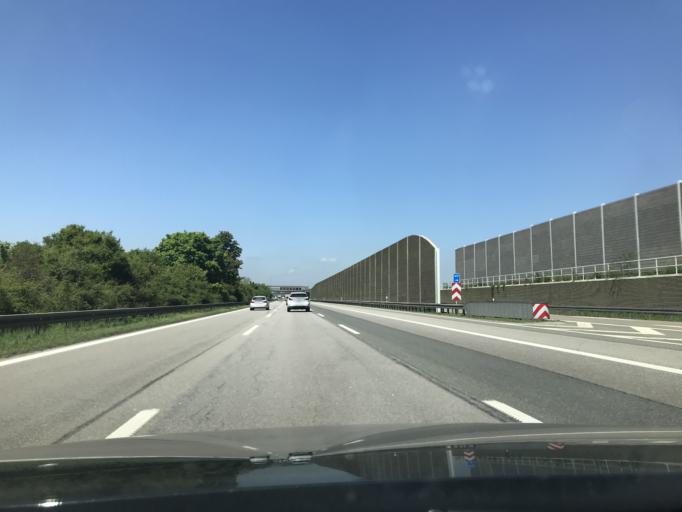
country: DE
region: Bavaria
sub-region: Upper Bavaria
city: Kirchheim bei Muenchen
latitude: 48.1662
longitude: 11.7419
